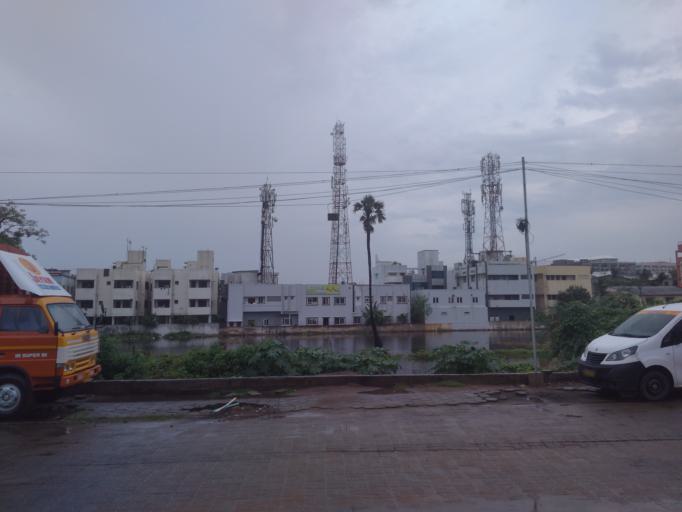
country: IN
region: Tamil Nadu
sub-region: Kancheepuram
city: Perungudi
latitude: 12.9423
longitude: 80.2362
